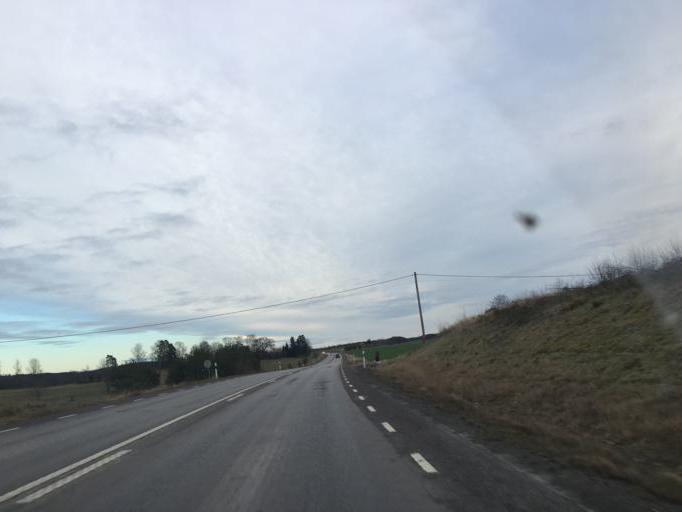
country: SE
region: OEstergoetland
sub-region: Norrkopings Kommun
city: Norrkoping
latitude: 58.4938
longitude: 16.2145
